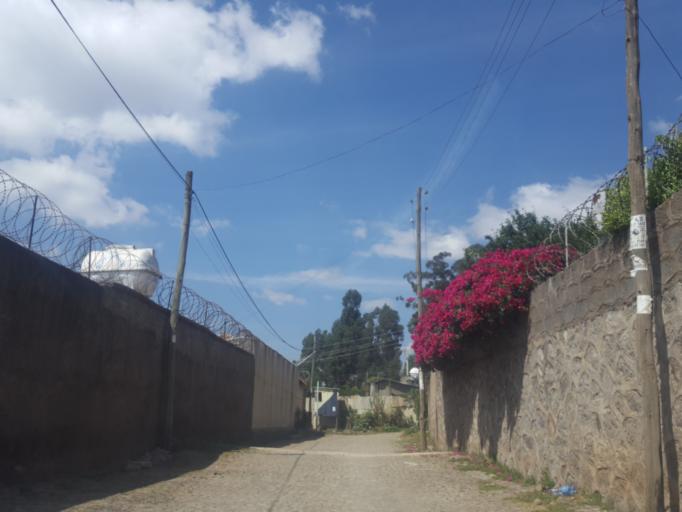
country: ET
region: Adis Abeba
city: Addis Ababa
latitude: 9.0507
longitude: 38.7295
